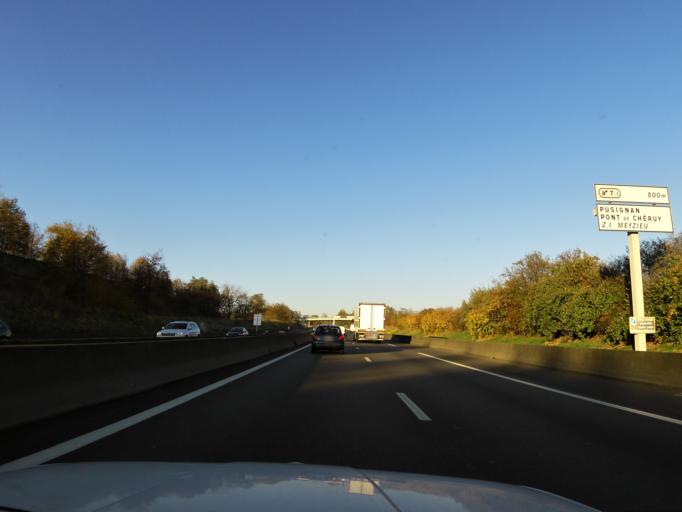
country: FR
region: Rhone-Alpes
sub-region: Departement du Rhone
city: Chassieu
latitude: 45.7389
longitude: 4.9847
